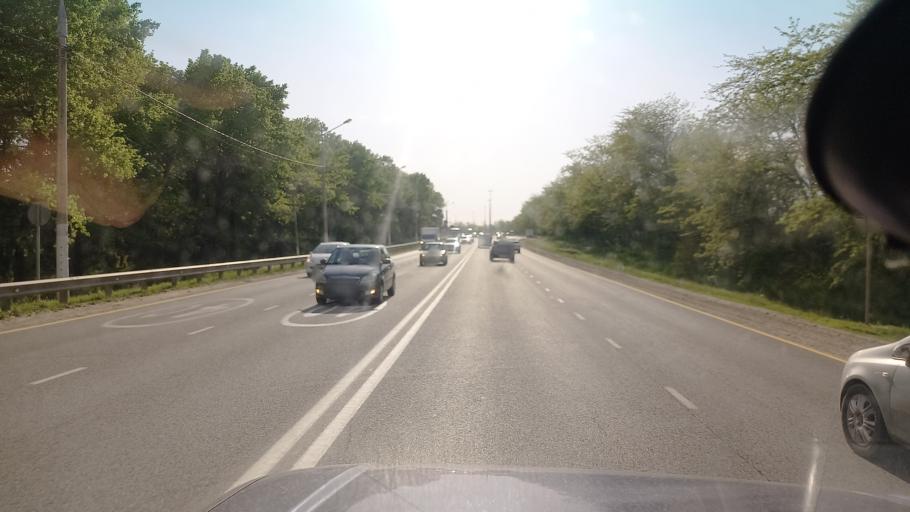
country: RU
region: Krasnodarskiy
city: Yelizavetinskaya
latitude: 45.0567
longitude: 38.8746
